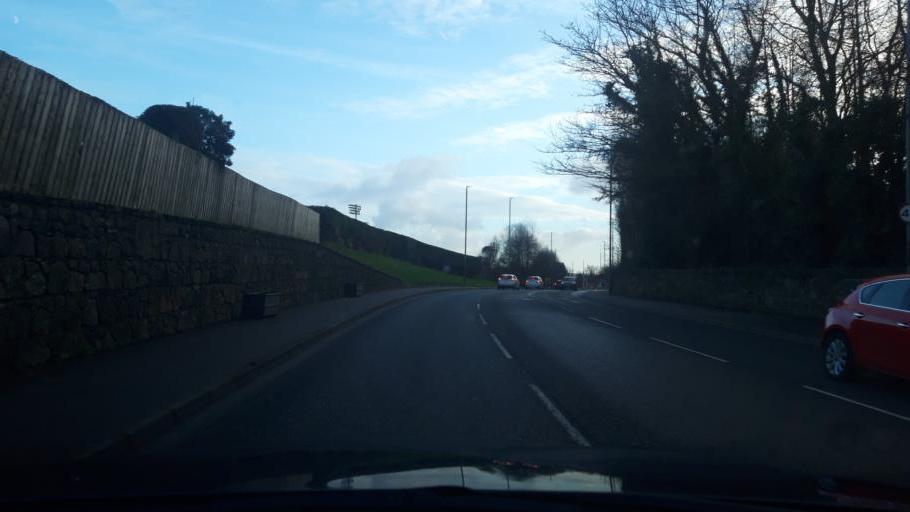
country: GB
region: Northern Ireland
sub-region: Dungannon District
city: Dungannon
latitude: 54.4910
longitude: -6.7492
